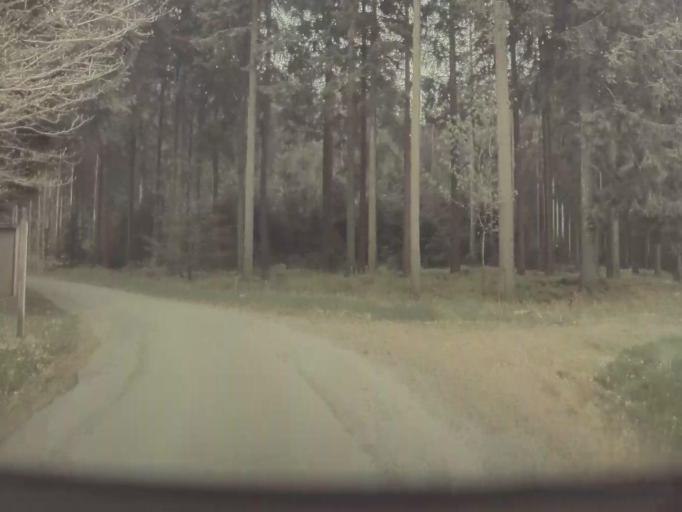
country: BE
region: Wallonia
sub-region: Province du Luxembourg
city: La Roche-en-Ardenne
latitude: 50.2380
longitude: 5.5950
